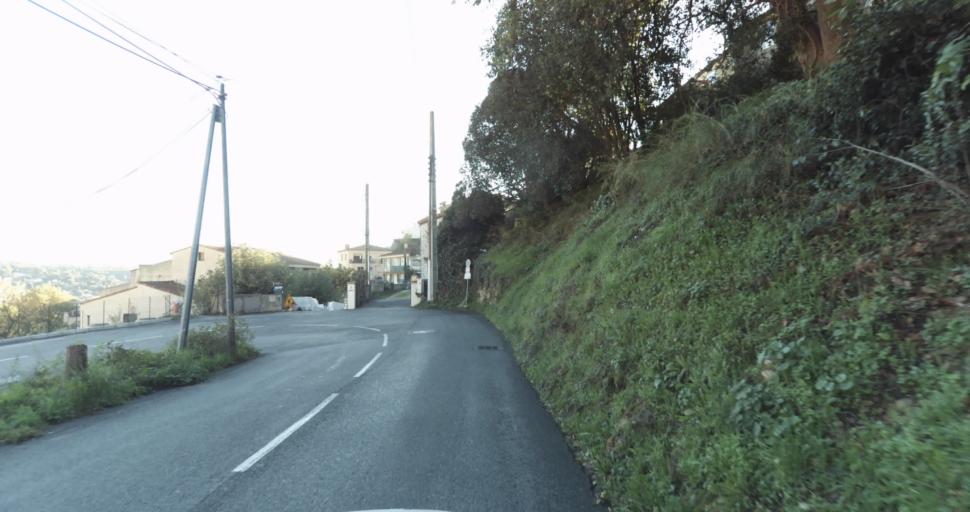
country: FR
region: Provence-Alpes-Cote d'Azur
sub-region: Departement des Alpes-Maritimes
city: Vence
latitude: 43.7230
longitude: 7.1160
